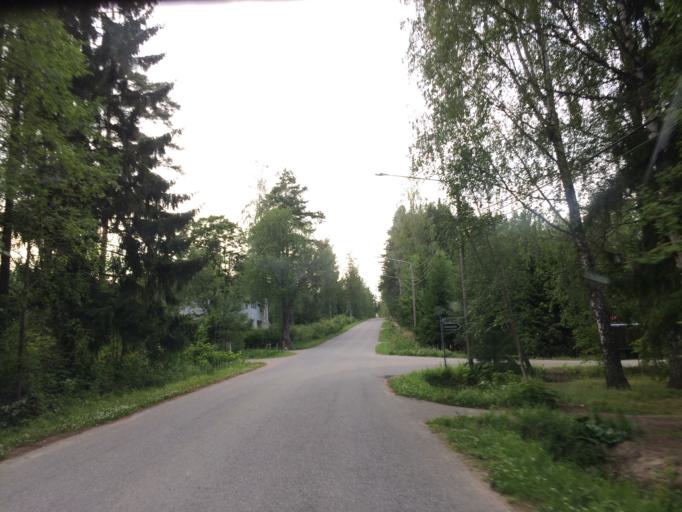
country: FI
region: Haeme
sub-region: Haemeenlinna
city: Tervakoski
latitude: 60.8501
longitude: 24.6216
